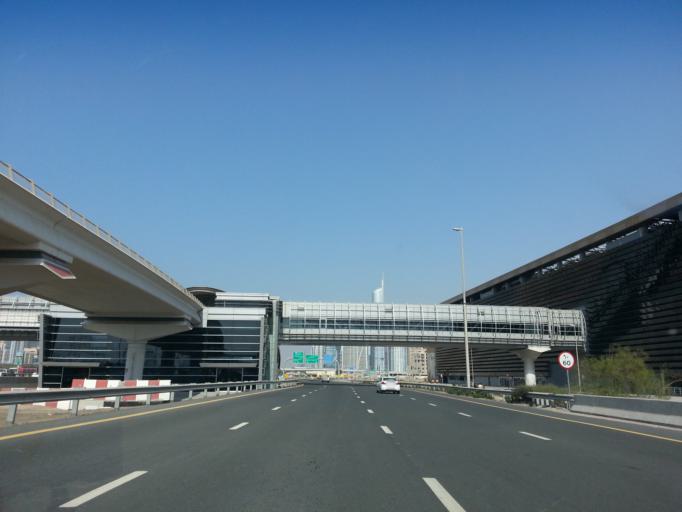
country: AE
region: Dubai
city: Dubai
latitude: 25.0567
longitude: 55.1263
